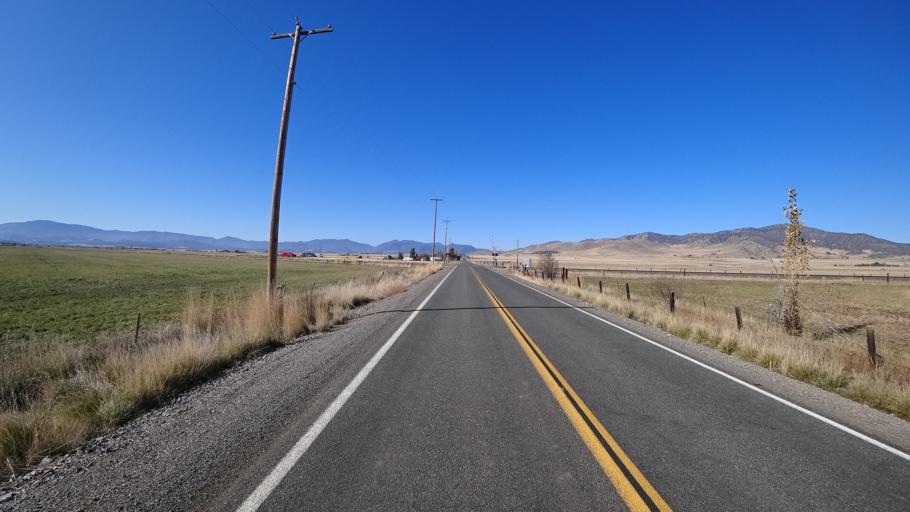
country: US
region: California
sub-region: Siskiyou County
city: Montague
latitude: 41.7705
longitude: -122.4906
